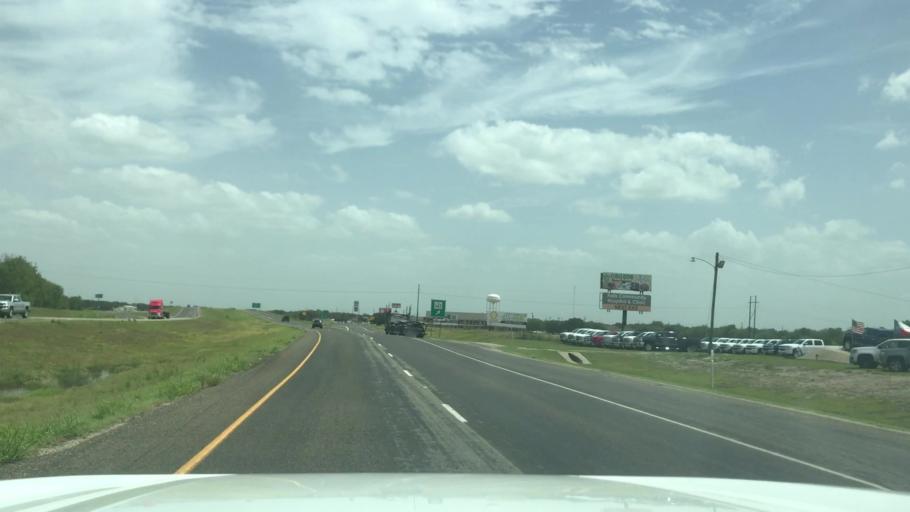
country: US
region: Texas
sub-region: Falls County
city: Marlin
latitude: 31.3250
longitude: -96.8870
